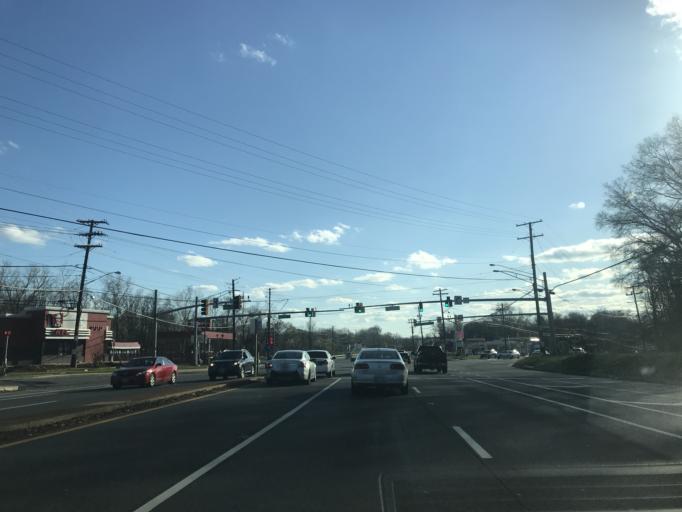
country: US
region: Maryland
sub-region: Prince George's County
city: Peppermill Village
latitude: 38.9101
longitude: -76.8915
